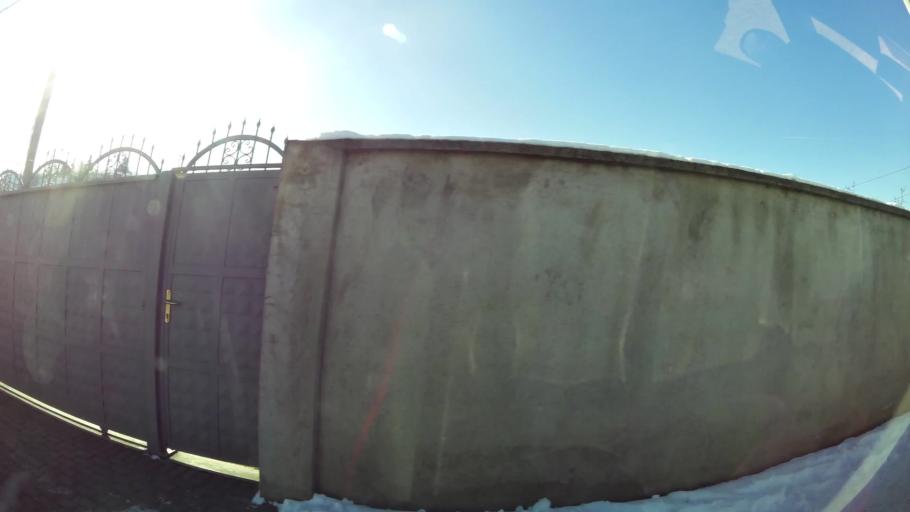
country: MK
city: Ljubin
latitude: 42.0021
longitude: 21.3140
